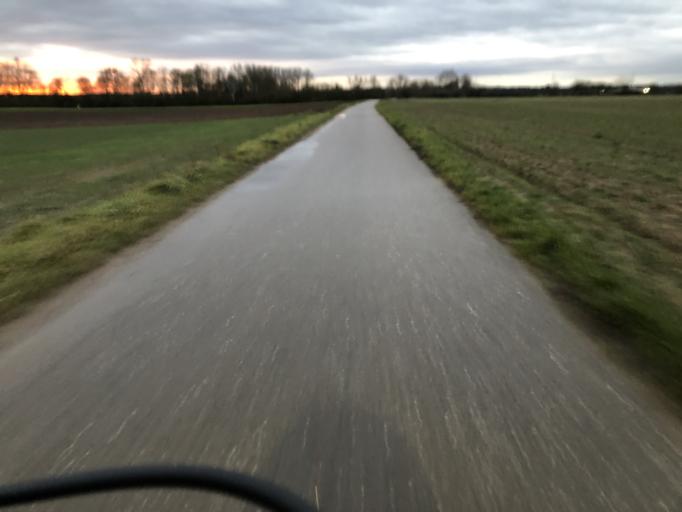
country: DE
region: Baden-Wuerttemberg
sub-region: Karlsruhe Region
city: Reilingen
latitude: 49.3020
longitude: 8.5419
